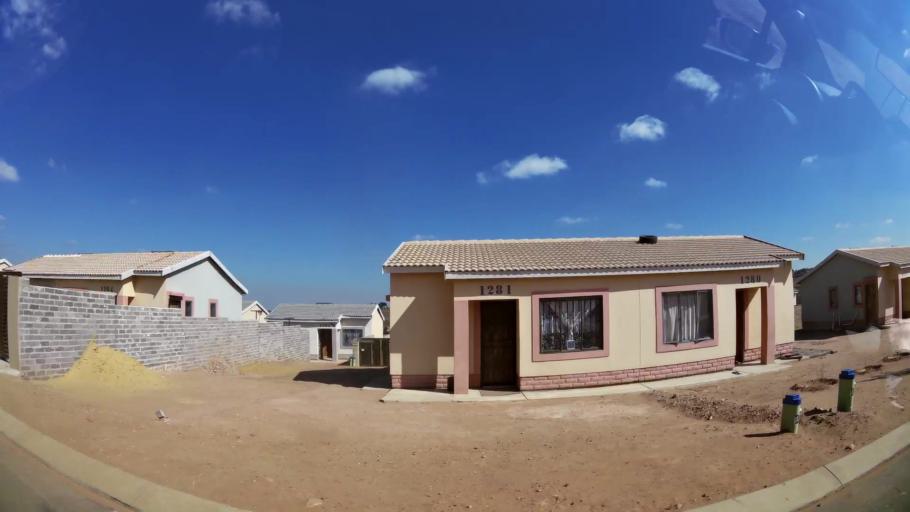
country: ZA
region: Gauteng
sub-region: West Rand District Municipality
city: Randfontein
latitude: -26.1671
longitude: 27.7688
